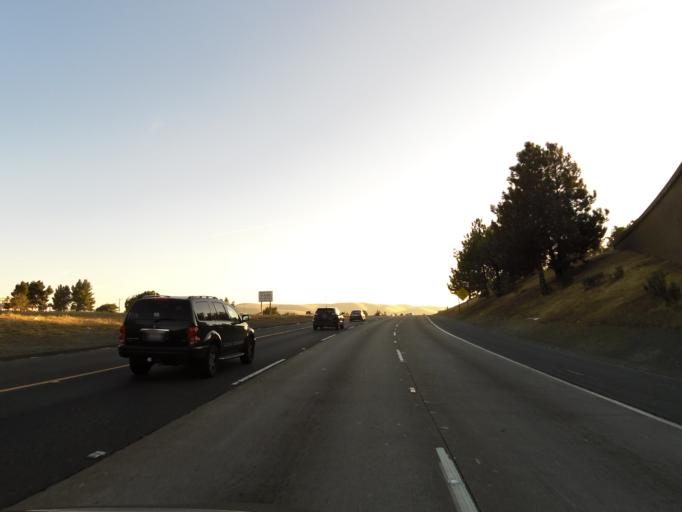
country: US
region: California
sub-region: Contra Costa County
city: Concord
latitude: 38.0060
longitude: -122.0351
